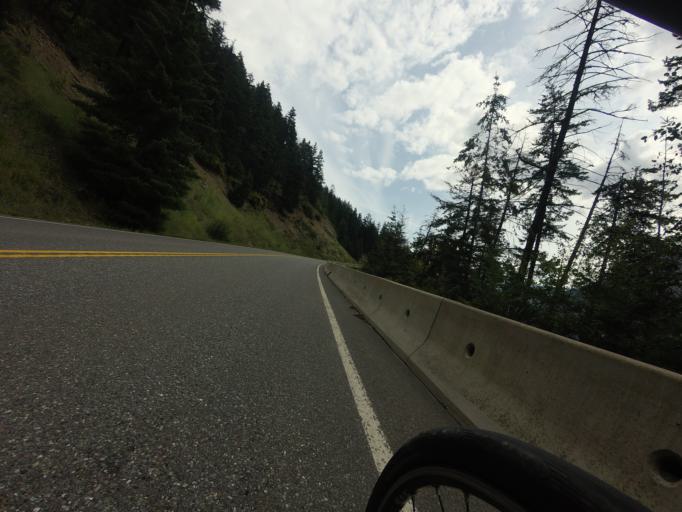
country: CA
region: British Columbia
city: Lillooet
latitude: 50.6481
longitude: -122.0222
